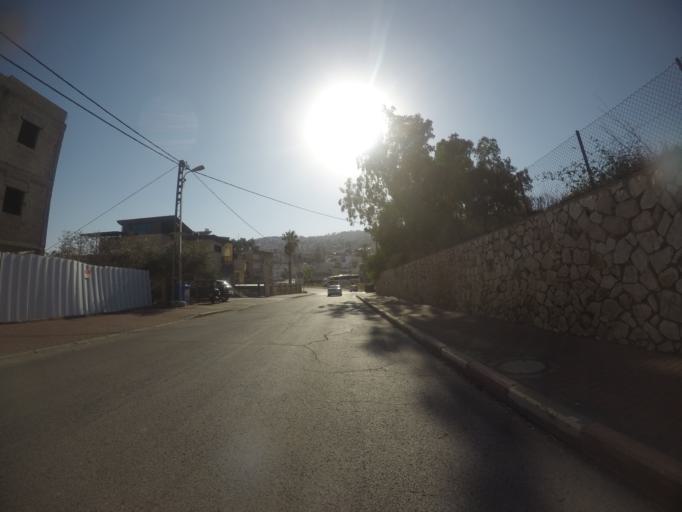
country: IL
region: Northern District
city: Tiberias
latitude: 32.7935
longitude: 35.5262
